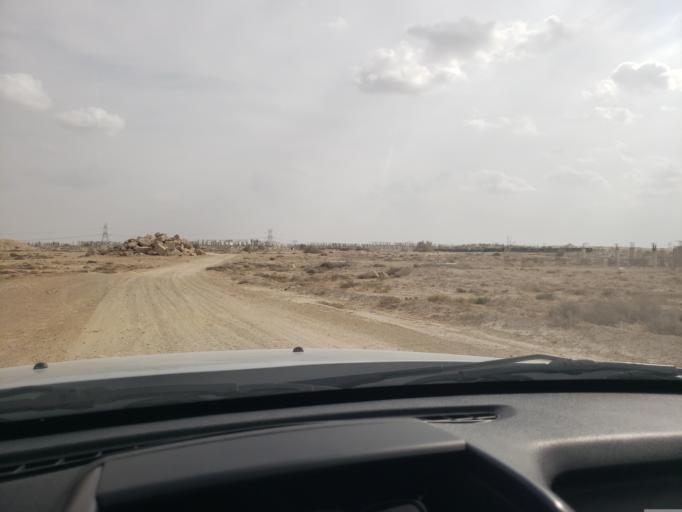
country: AE
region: Dubai
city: Dubai
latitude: 24.9997
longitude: 55.2442
